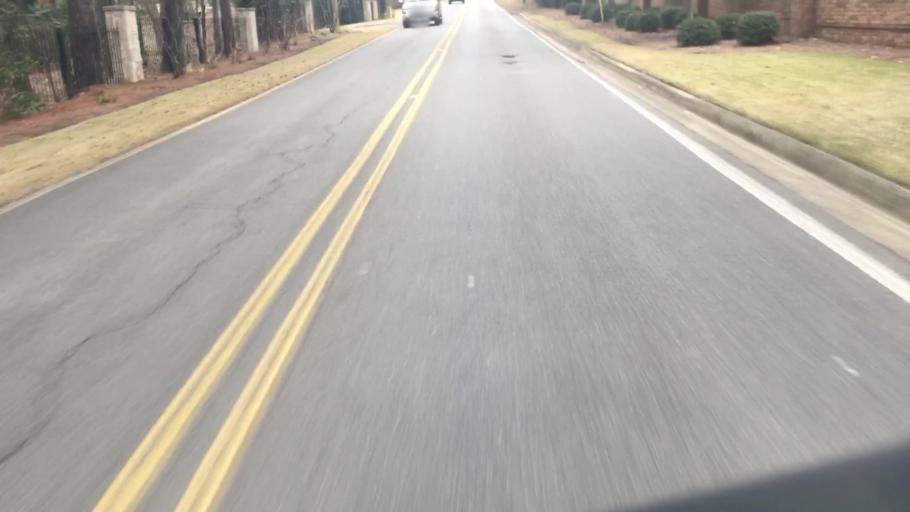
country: US
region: Alabama
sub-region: Jefferson County
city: Vestavia Hills
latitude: 33.4218
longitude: -86.7583
